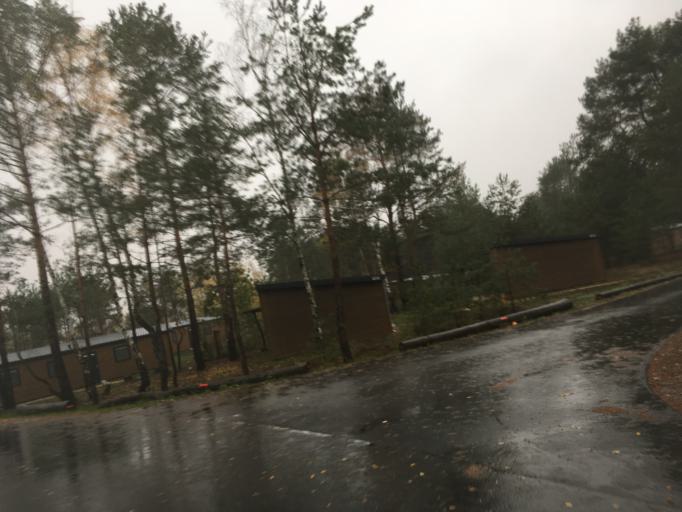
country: DE
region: Brandenburg
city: Halbe
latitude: 52.0349
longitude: 13.7341
